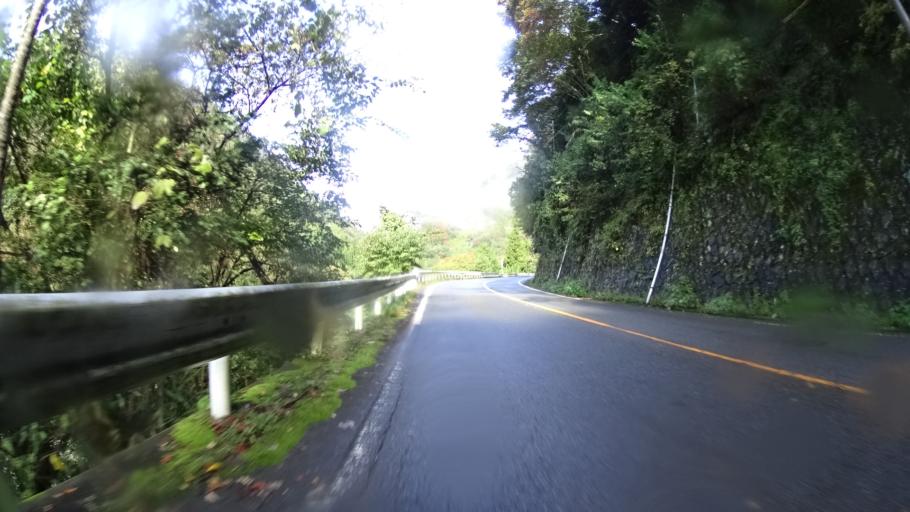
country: JP
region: Yamanashi
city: Otsuki
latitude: 35.7807
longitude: 138.9789
